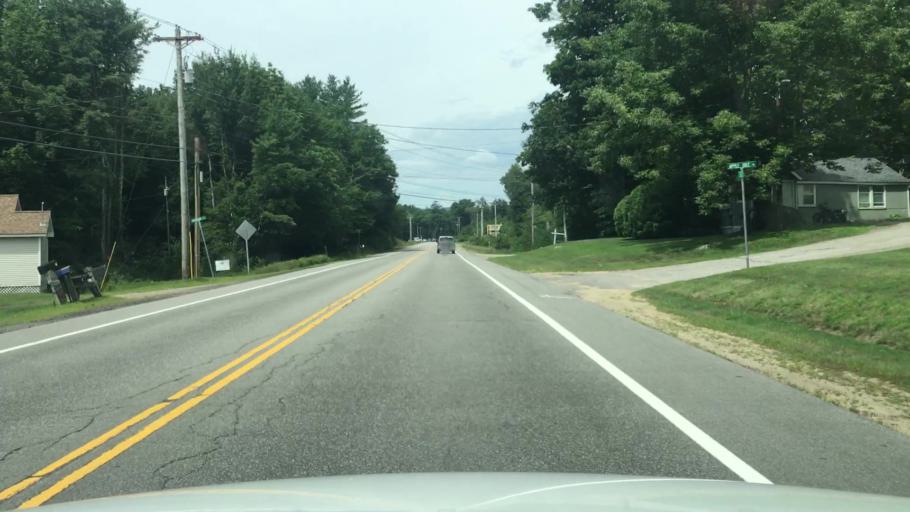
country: US
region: New Hampshire
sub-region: Grafton County
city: Ashland
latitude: 43.6213
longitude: -71.5964
